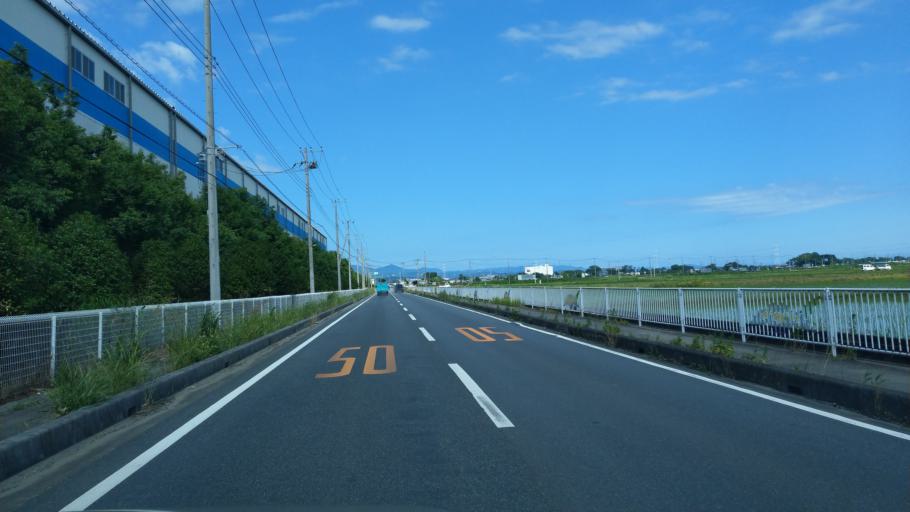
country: JP
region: Saitama
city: Sakado
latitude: 35.9884
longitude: 139.4631
